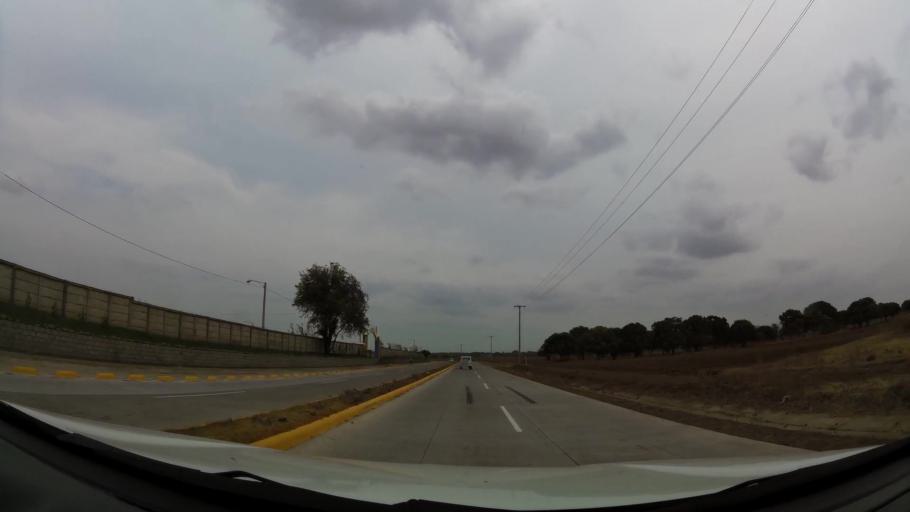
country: NI
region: Managua
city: Managua
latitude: 12.1063
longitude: -86.1743
